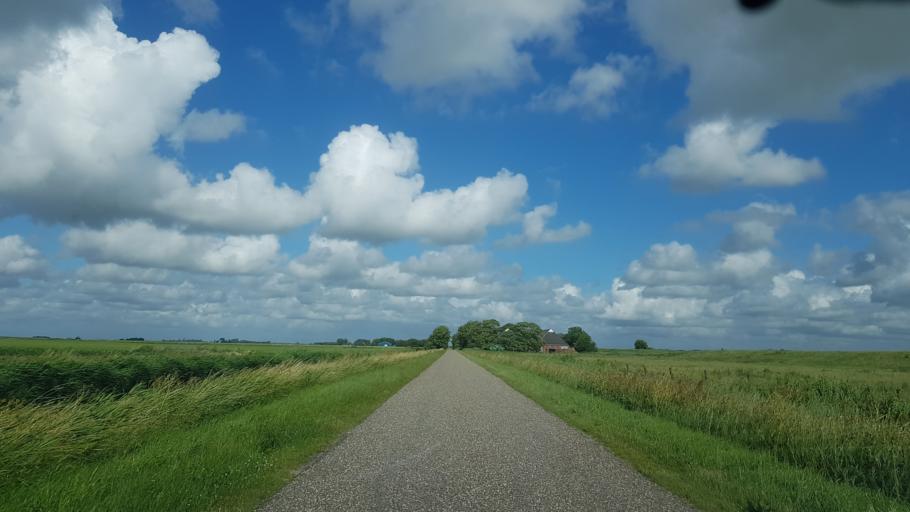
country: NL
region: Groningen
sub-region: Gemeente Winsum
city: Winsum
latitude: 53.4065
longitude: 6.5448
